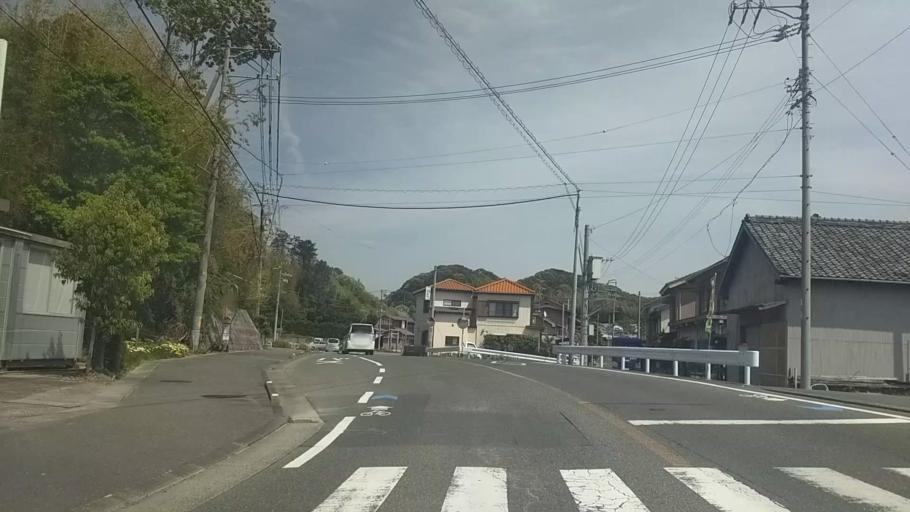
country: JP
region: Shizuoka
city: Kosai-shi
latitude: 34.7886
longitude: 137.6032
